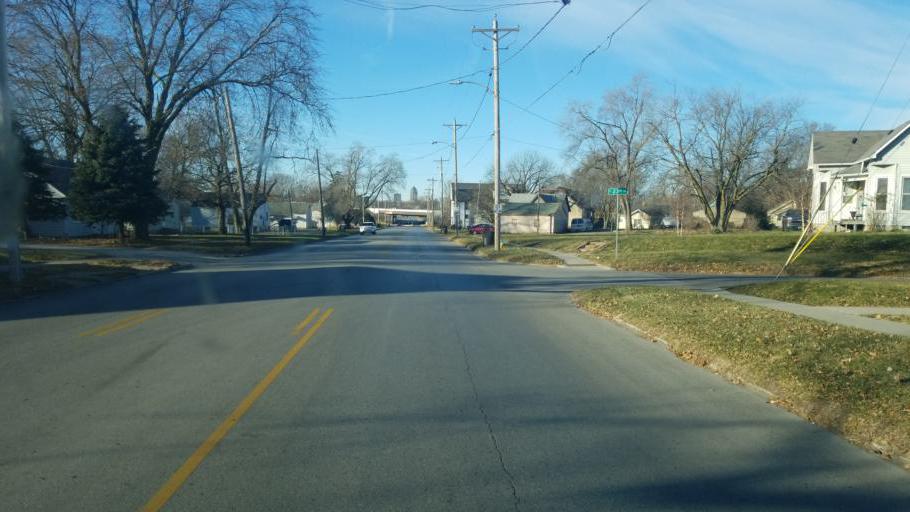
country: US
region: Iowa
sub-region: Polk County
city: Des Moines
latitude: 41.6060
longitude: -93.5747
